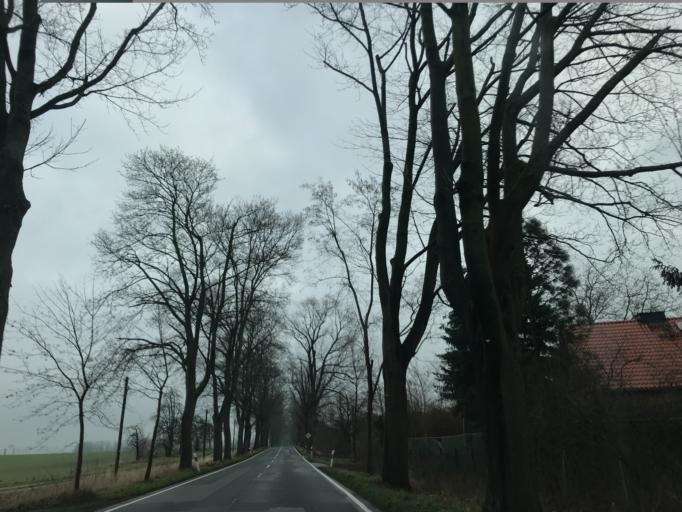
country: DE
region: Brandenburg
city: Kremmen
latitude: 52.7503
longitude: 12.9875
